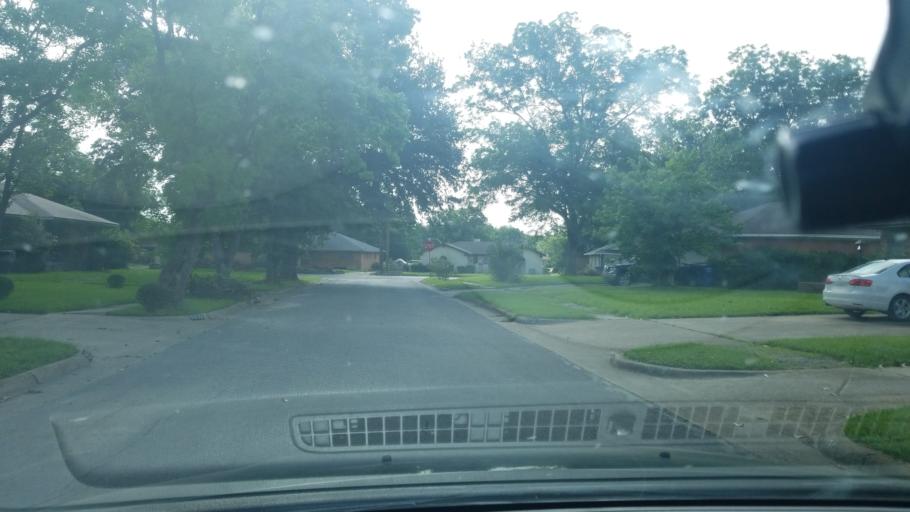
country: US
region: Texas
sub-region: Dallas County
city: Balch Springs
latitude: 32.7446
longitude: -96.6644
